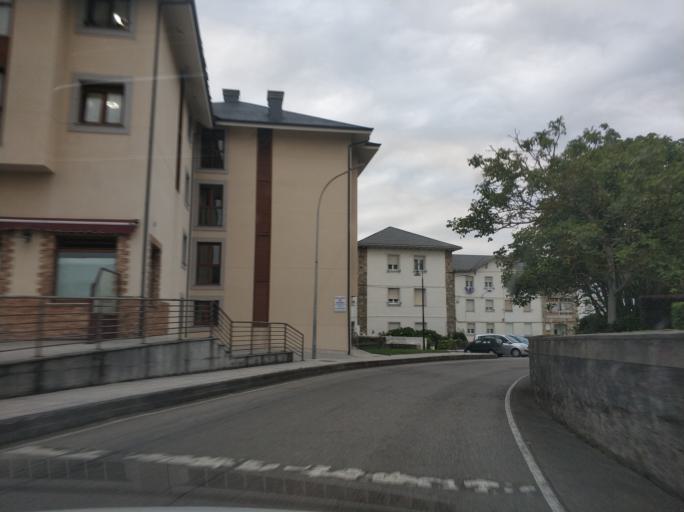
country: ES
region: Asturias
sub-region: Province of Asturias
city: Navia
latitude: 43.5453
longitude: -6.5296
